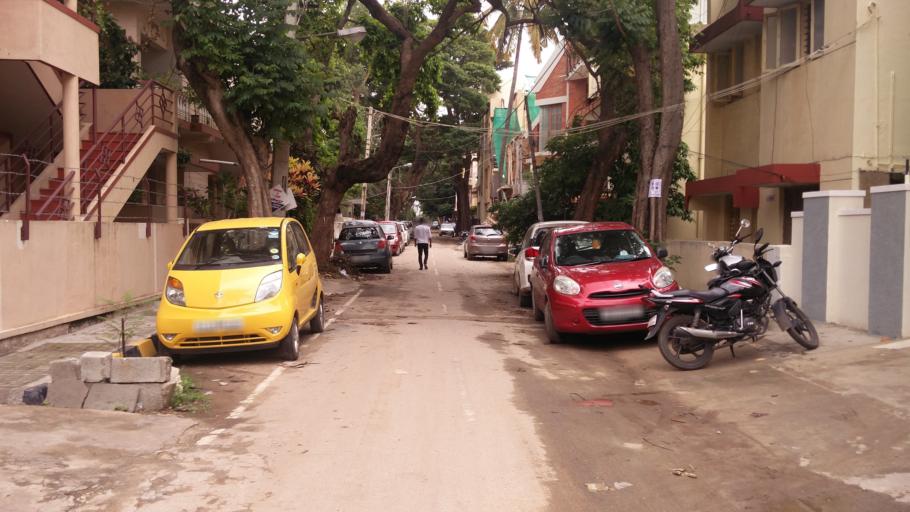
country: IN
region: Karnataka
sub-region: Bangalore Urban
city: Bangalore
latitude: 12.9777
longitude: 77.6336
